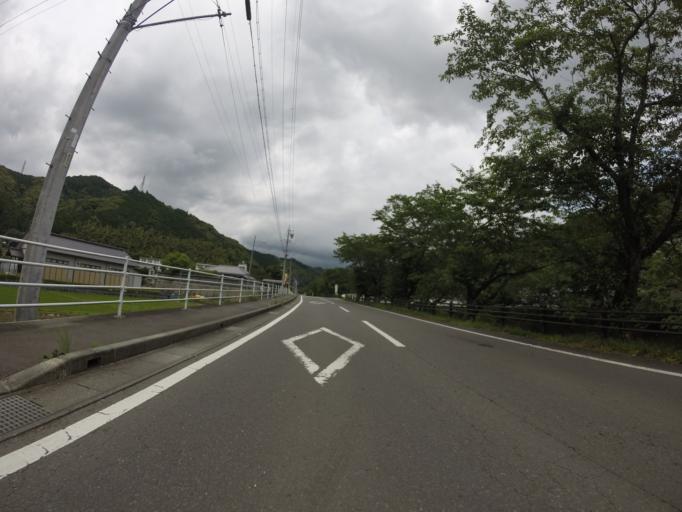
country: JP
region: Shizuoka
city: Shizuoka-shi
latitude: 34.9924
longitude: 138.3079
